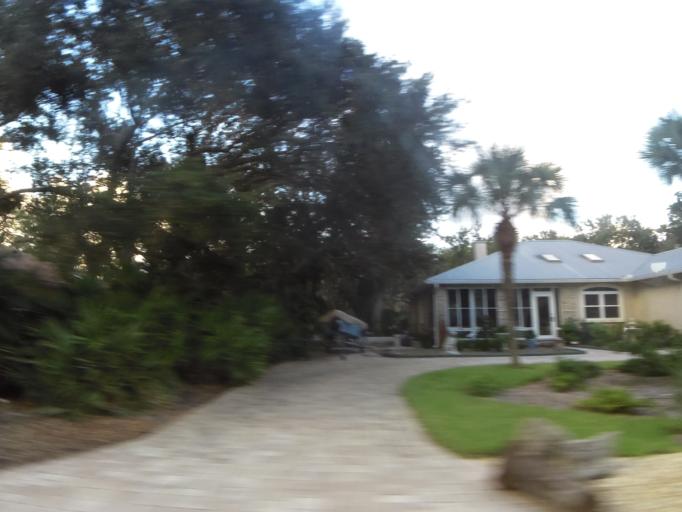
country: US
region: Florida
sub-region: Saint Johns County
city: Villano Beach
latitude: 29.9537
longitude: -81.3095
